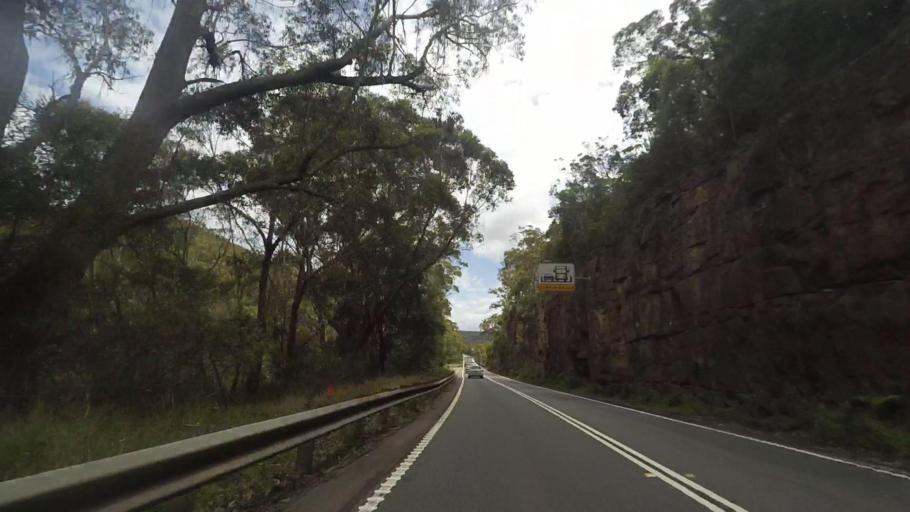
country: AU
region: New South Wales
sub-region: Sutherland Shire
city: Engadine
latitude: -34.0640
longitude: 150.9965
